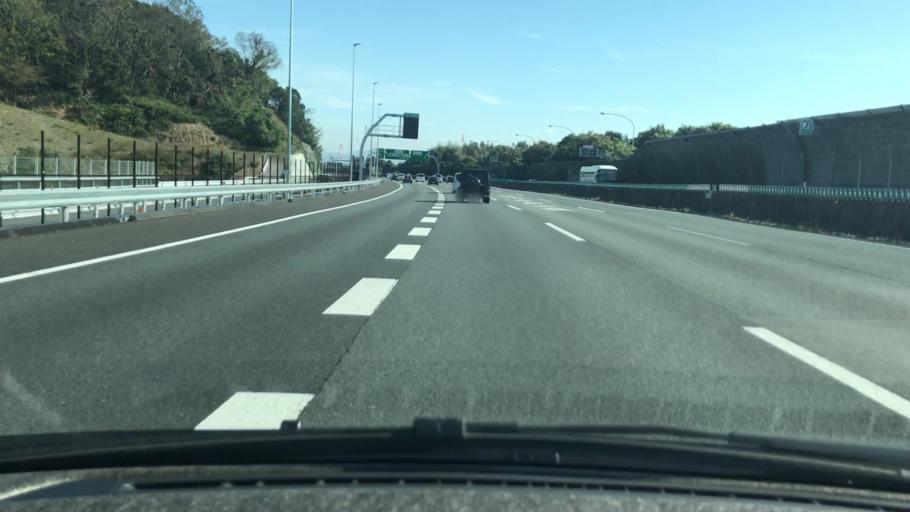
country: JP
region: Osaka
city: Takatsuki
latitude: 34.8633
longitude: 135.6375
